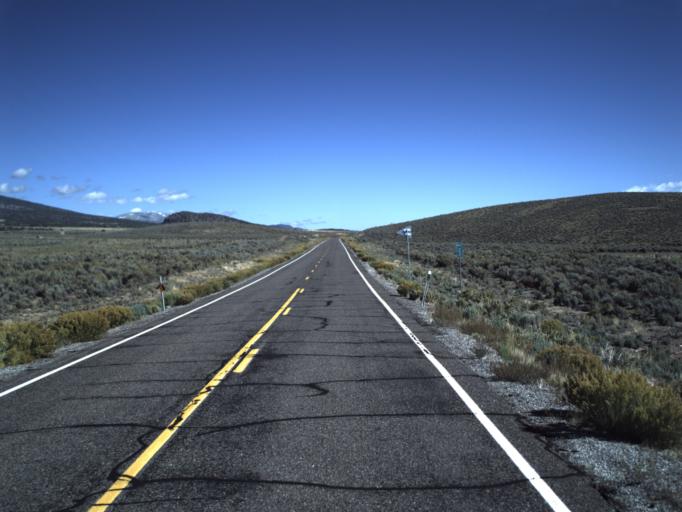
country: US
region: Utah
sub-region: Piute County
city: Junction
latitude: 38.3100
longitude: -111.9681
